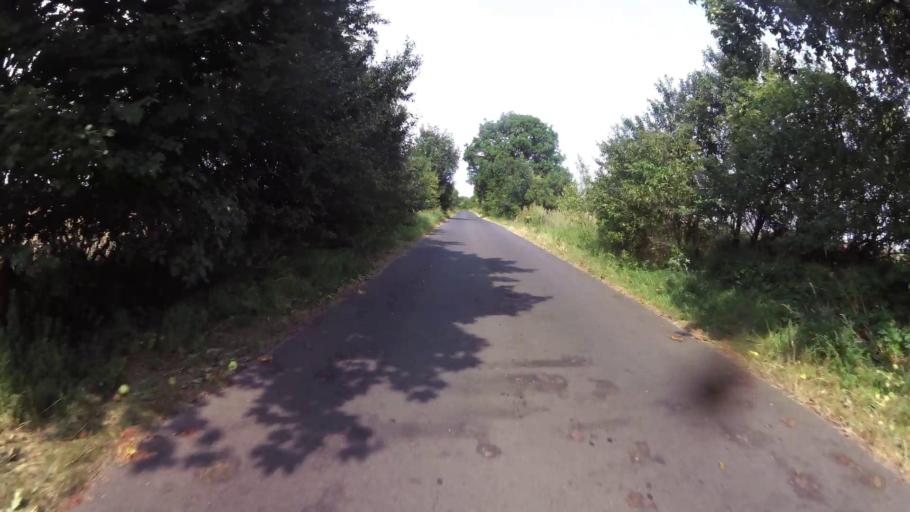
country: PL
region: West Pomeranian Voivodeship
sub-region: Powiat mysliborski
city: Nowogrodek Pomorski
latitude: 52.9695
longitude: 15.0226
